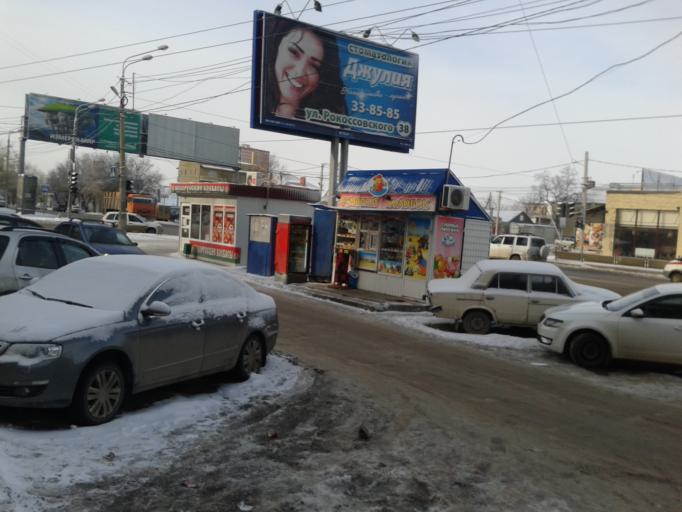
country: RU
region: Volgograd
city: Volgograd
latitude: 48.7225
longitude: 44.5121
